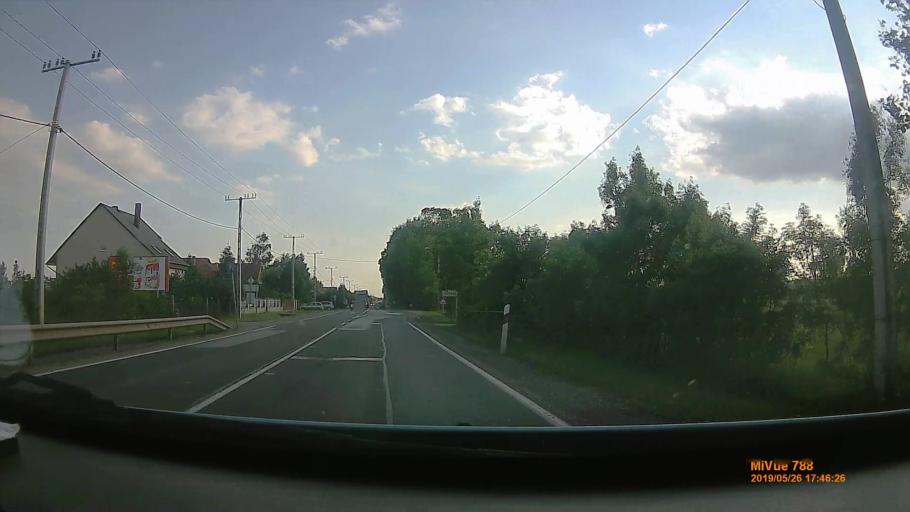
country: HU
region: Borsod-Abauj-Zemplen
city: Szikszo
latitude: 48.2085
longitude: 20.9388
